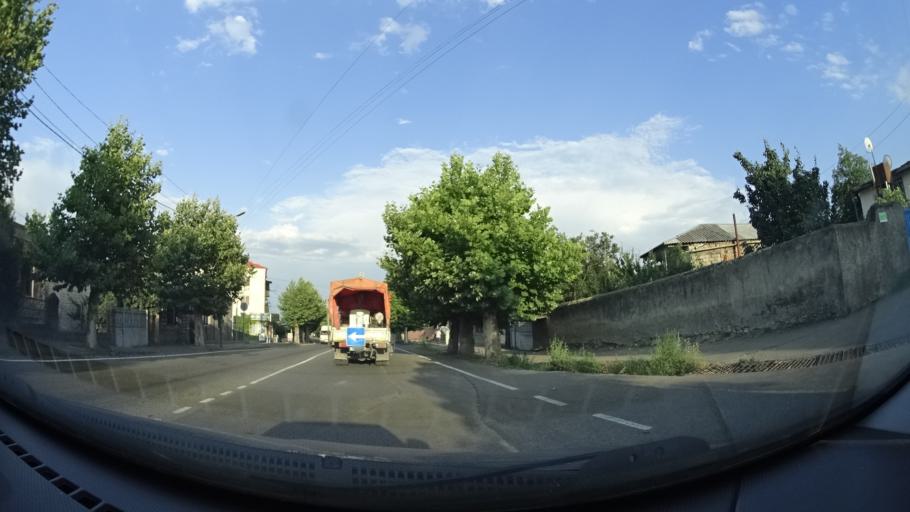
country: GE
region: Kakheti
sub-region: Telavi
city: Telavi
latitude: 41.9188
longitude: 45.4866
